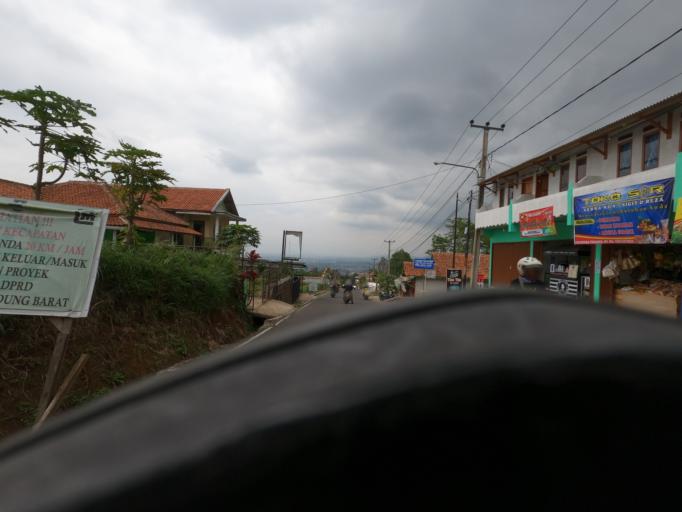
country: ID
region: West Java
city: Padalarang
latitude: -6.8346
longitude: 107.5159
